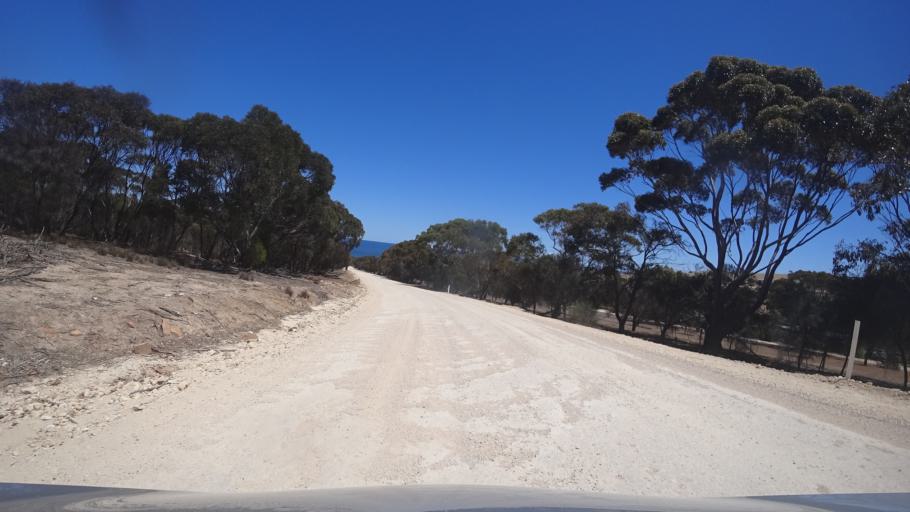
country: AU
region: South Australia
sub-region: Kangaroo Island
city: Kingscote
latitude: -35.6262
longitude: 137.2116
